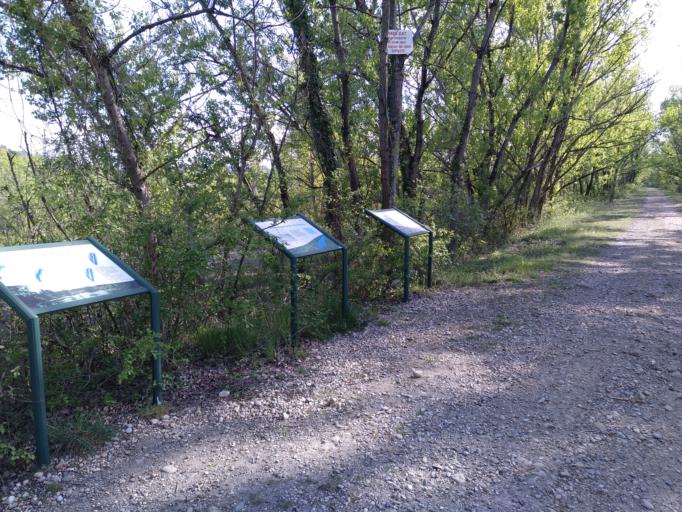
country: FR
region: Rhone-Alpes
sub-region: Departement du Rhone
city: Vernaison
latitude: 45.6404
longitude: 4.8200
